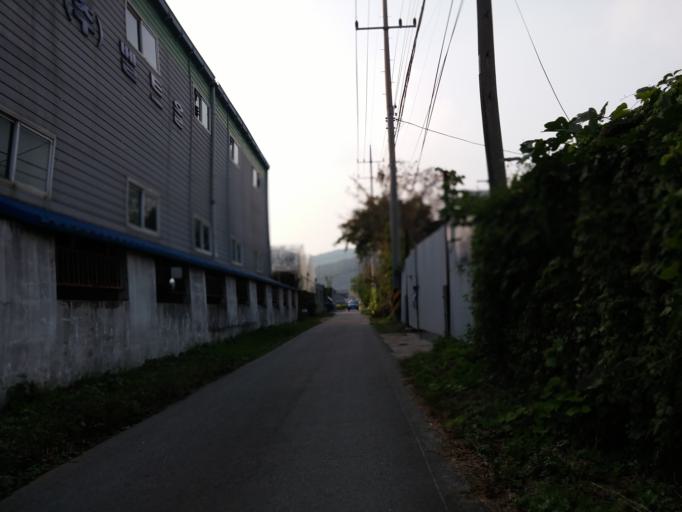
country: KR
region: Chungcheongbuk-do
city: Okcheon
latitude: 36.3335
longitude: 127.5271
